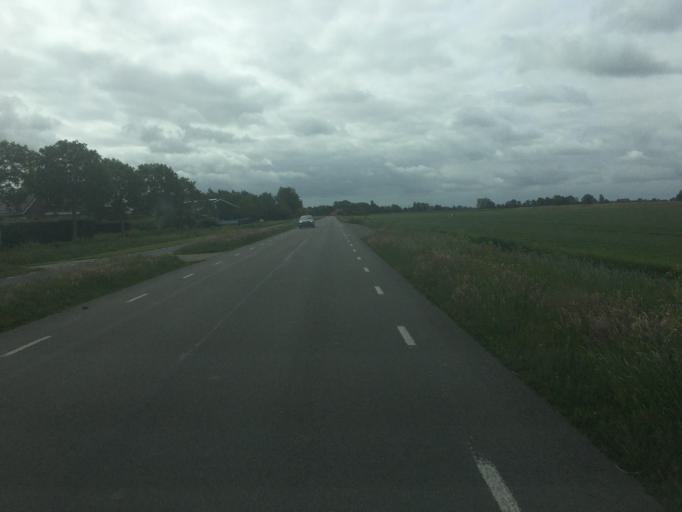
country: NL
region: Friesland
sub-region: Gemeente Lemsterland
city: Echtenerbrug
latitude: 52.8985
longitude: 5.8455
